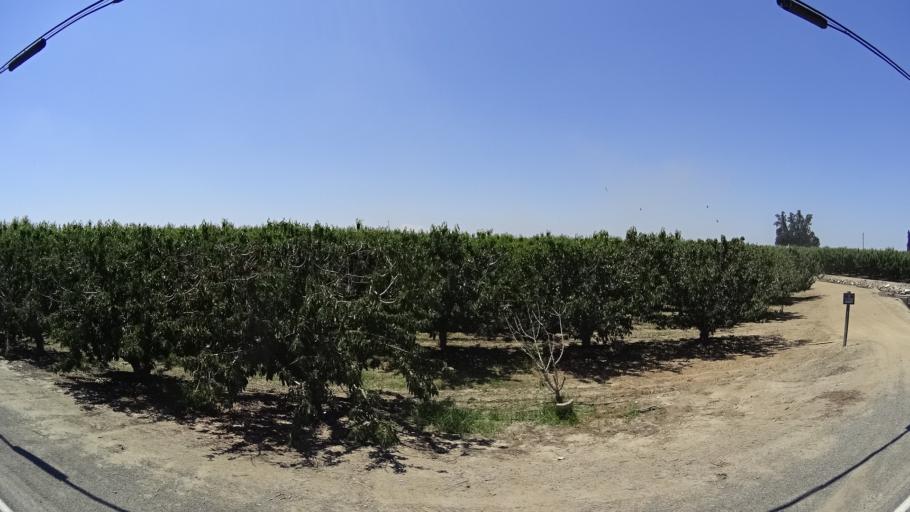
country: US
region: California
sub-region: Kings County
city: Lucerne
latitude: 36.3814
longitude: -119.6550
